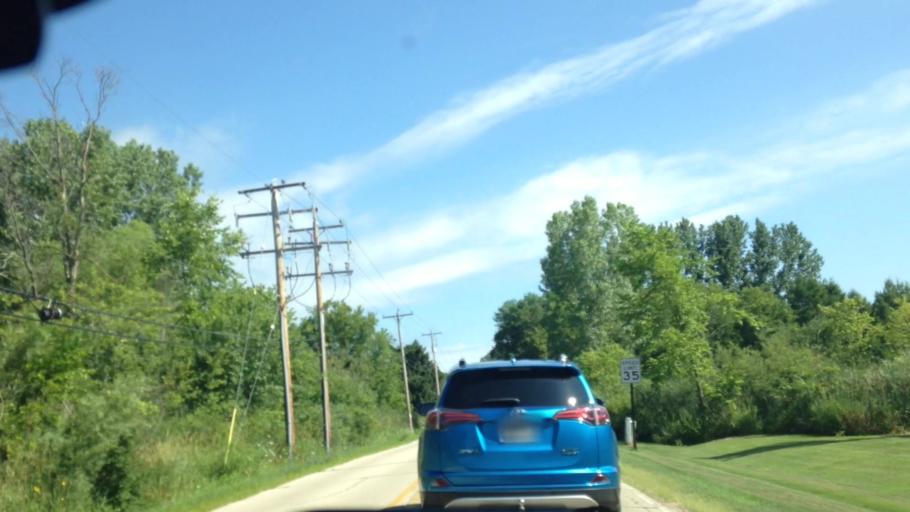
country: US
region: Wisconsin
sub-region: Washington County
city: West Bend
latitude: 43.4134
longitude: -88.2260
